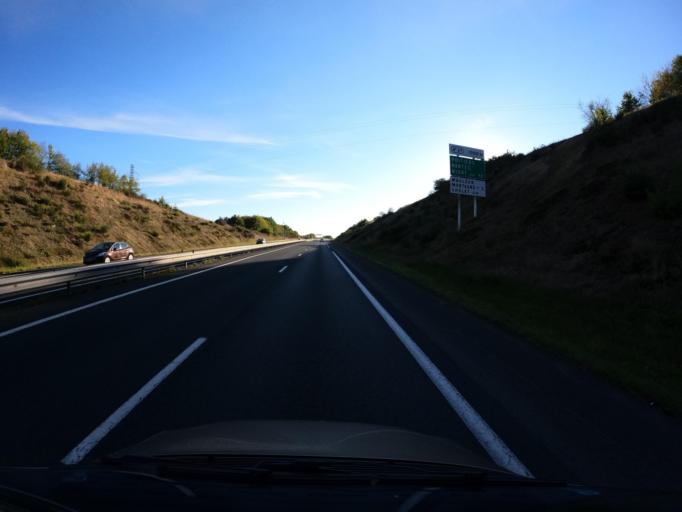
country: FR
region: Pays de la Loire
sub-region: Departement de Maine-et-Loire
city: La Tessoualle
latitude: 47.0253
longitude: -0.8659
